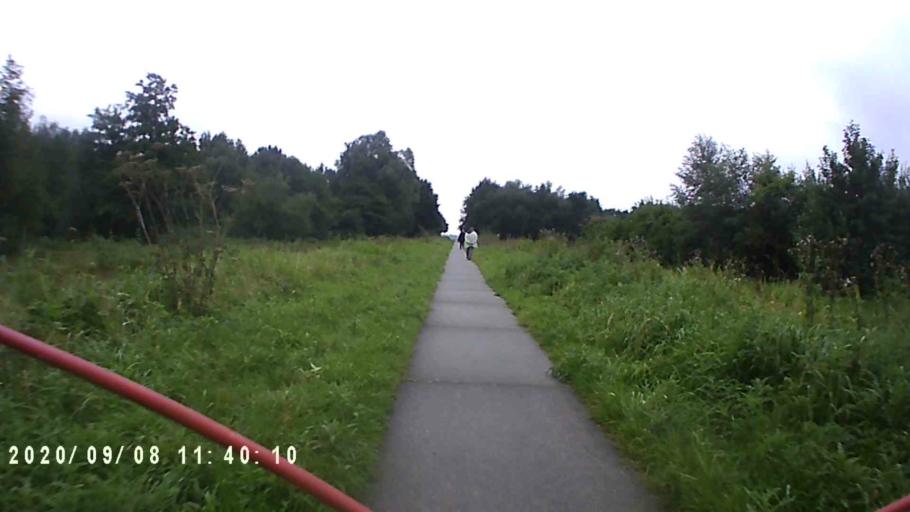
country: NL
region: Groningen
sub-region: Gemeente Hoogezand-Sappemeer
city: Sappemeer
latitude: 53.1528
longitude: 6.7841
